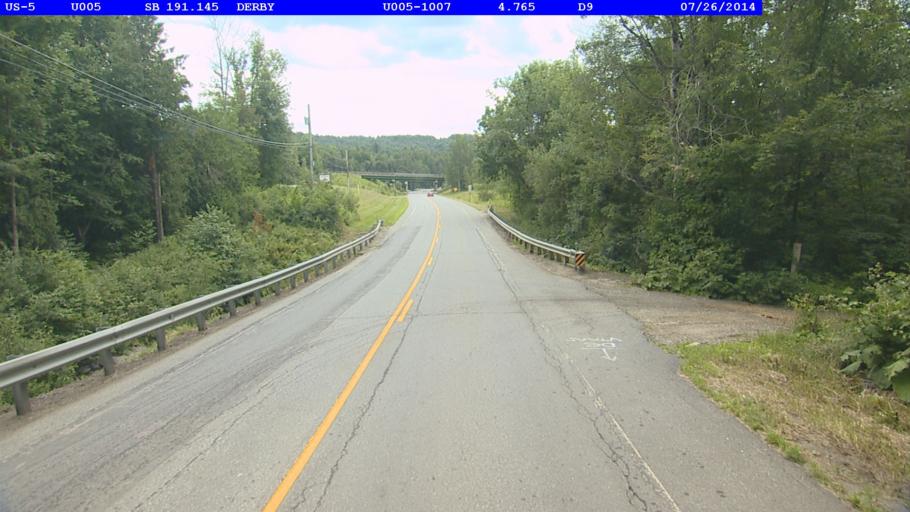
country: US
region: Vermont
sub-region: Orleans County
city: Newport
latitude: 44.9900
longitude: -72.1065
